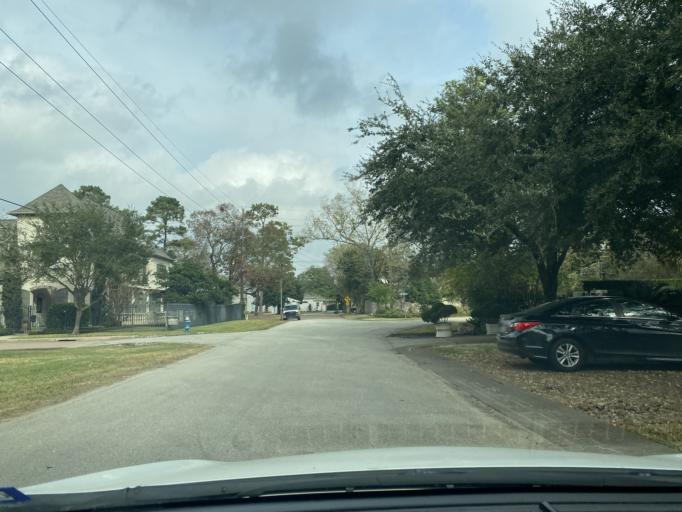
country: US
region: Texas
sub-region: Harris County
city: Hunters Creek Village
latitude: 29.7652
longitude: -95.4748
